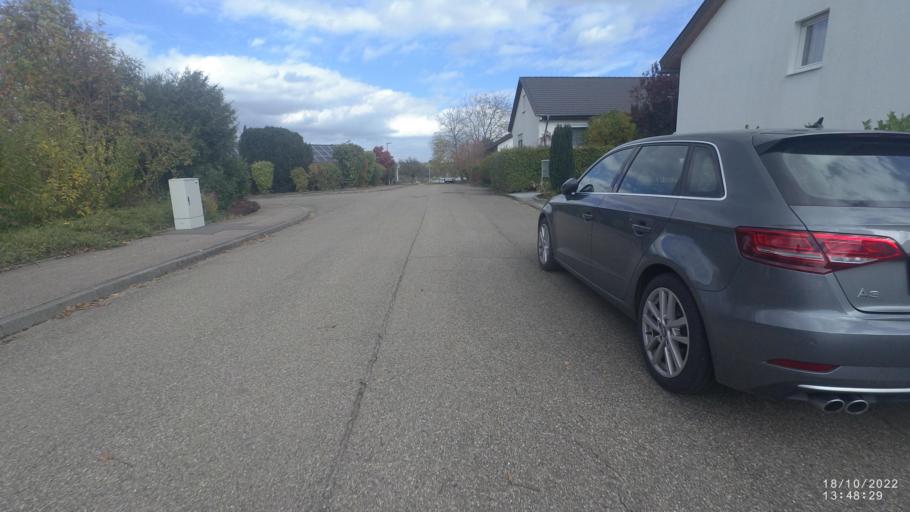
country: DE
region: Baden-Wuerttemberg
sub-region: Regierungsbezirk Stuttgart
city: Zell unter Aichelberg
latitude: 48.6491
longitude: 9.5800
